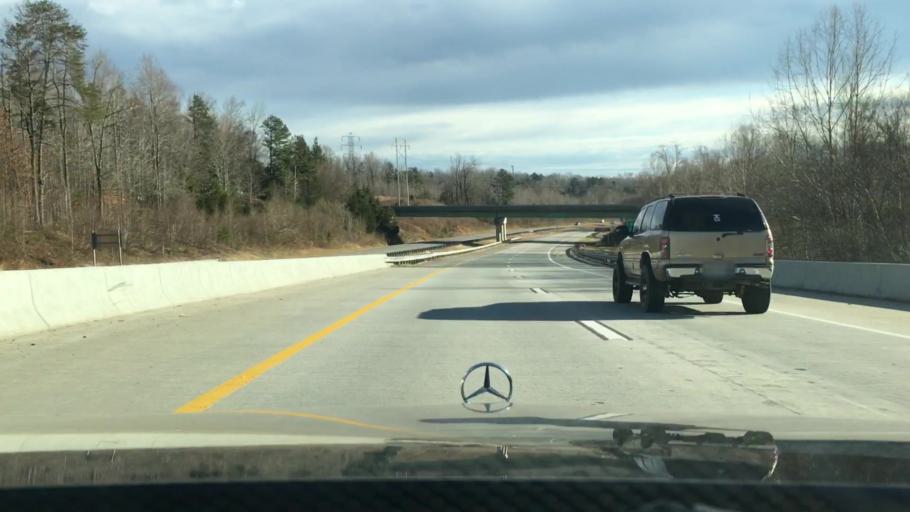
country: US
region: Virginia
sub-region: City of Danville
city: Danville
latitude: 36.6102
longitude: -79.3598
